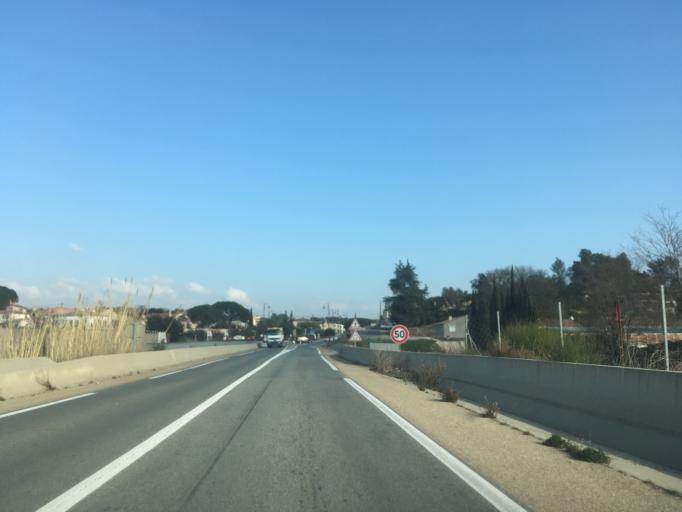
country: FR
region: Provence-Alpes-Cote d'Azur
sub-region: Departement du Var
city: Vidauban
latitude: 43.4294
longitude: 6.4360
